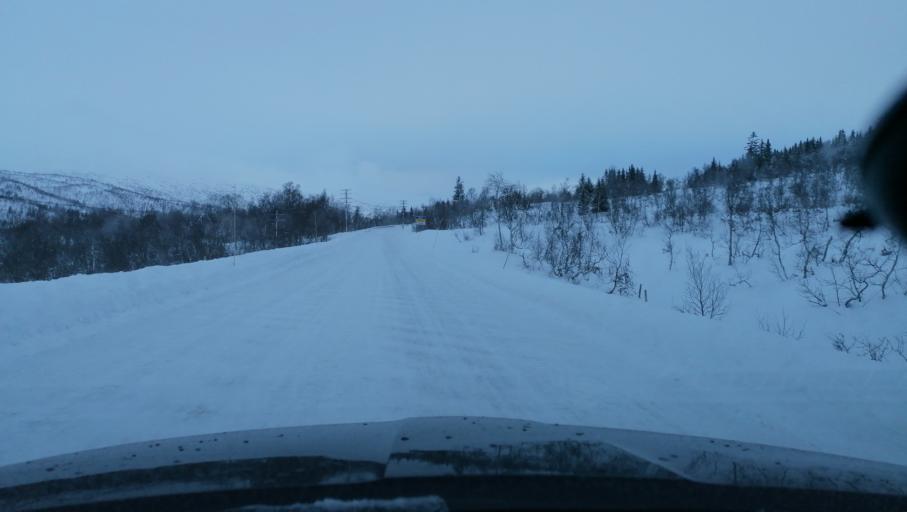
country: NO
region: Aust-Agder
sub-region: Bykle
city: Hovden
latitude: 59.6370
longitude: 7.4539
